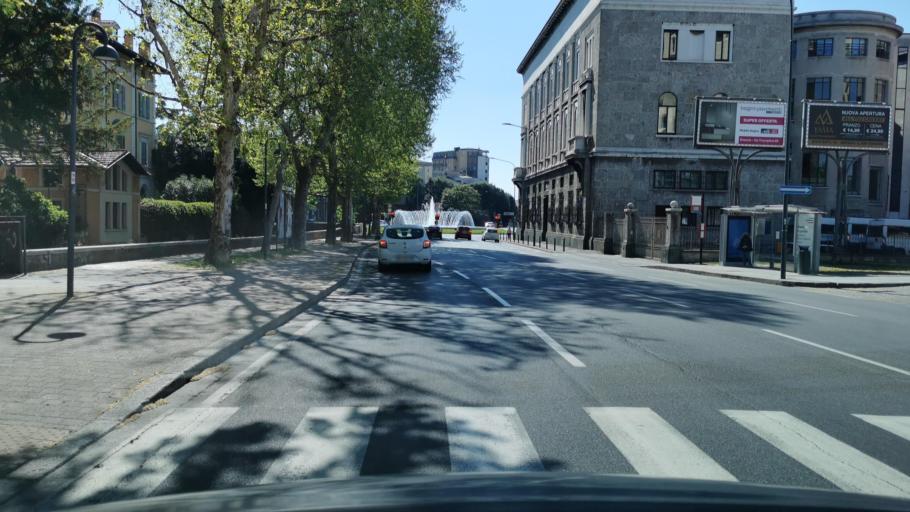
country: IT
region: Lombardy
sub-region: Provincia di Brescia
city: Brescia
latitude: 45.5359
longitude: 10.2105
